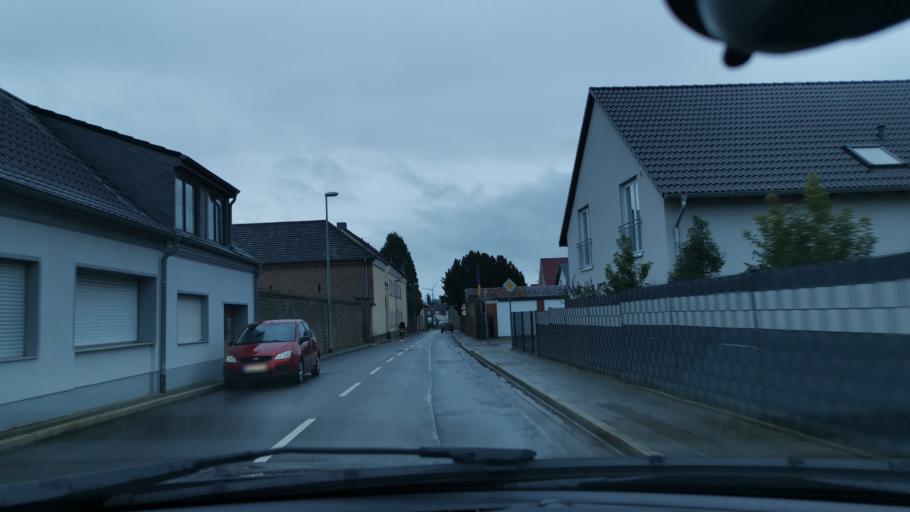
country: DE
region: North Rhine-Westphalia
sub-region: Regierungsbezirk Koln
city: Titz
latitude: 51.0005
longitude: 6.4877
